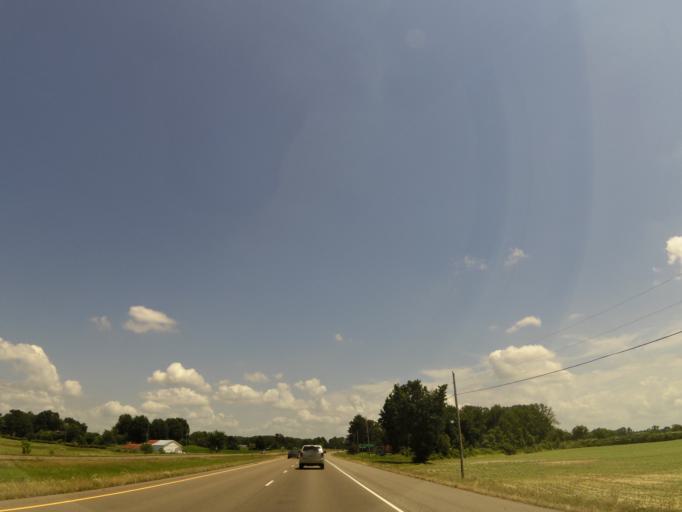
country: US
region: Tennessee
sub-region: Crockett County
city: Alamo
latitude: 35.8536
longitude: -89.1987
